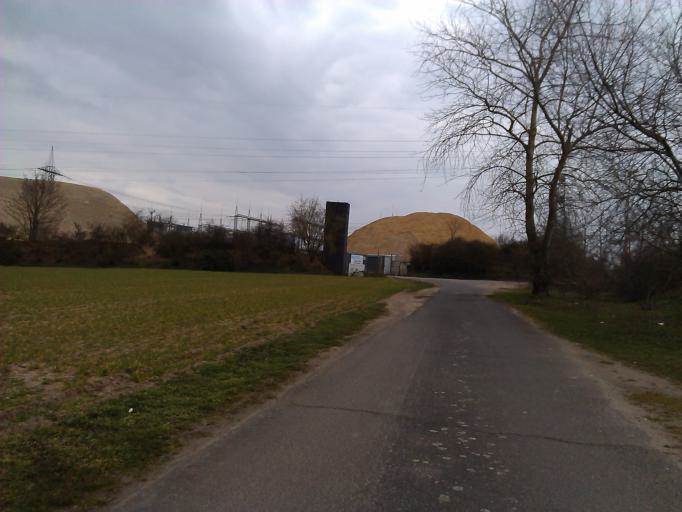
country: DE
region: Hesse
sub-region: Regierungsbezirk Darmstadt
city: Bischofsheim
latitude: 49.9798
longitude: 8.3855
